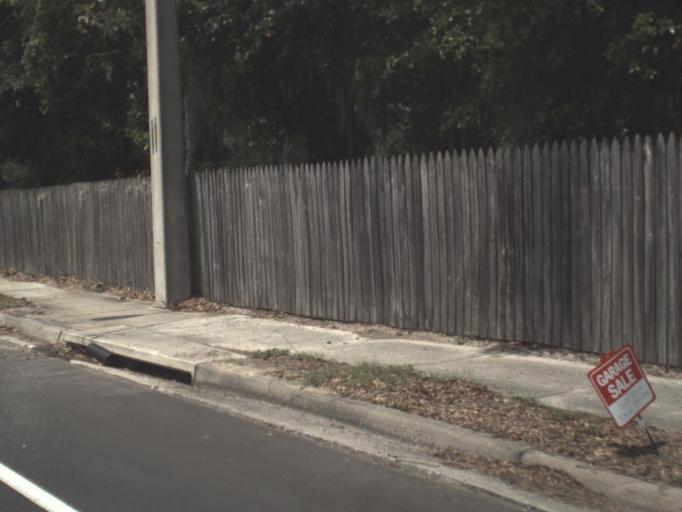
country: US
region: Florida
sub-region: Clay County
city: Orange Park
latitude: 30.2224
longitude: -81.6157
